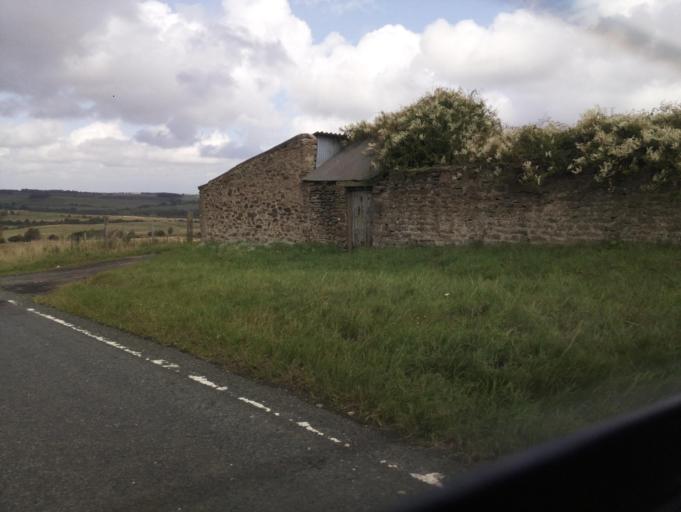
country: GB
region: England
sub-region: County Durham
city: Tow Law
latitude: 54.7813
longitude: -1.8554
